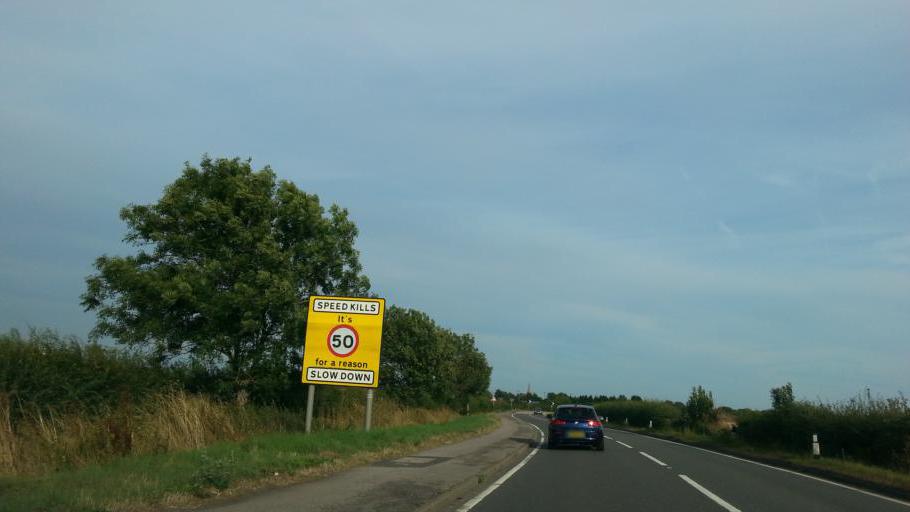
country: GB
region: England
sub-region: Nottinghamshire
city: Newark on Trent
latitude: 53.0879
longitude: -0.8383
